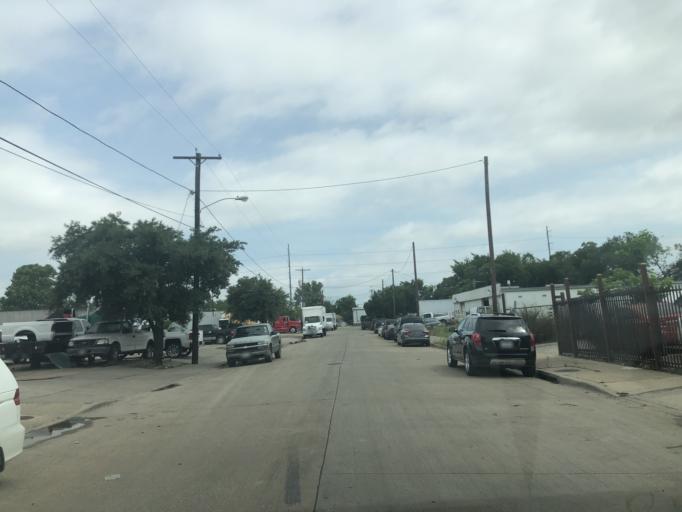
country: US
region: Texas
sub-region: Dallas County
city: Cockrell Hill
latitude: 32.8051
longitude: -96.8763
